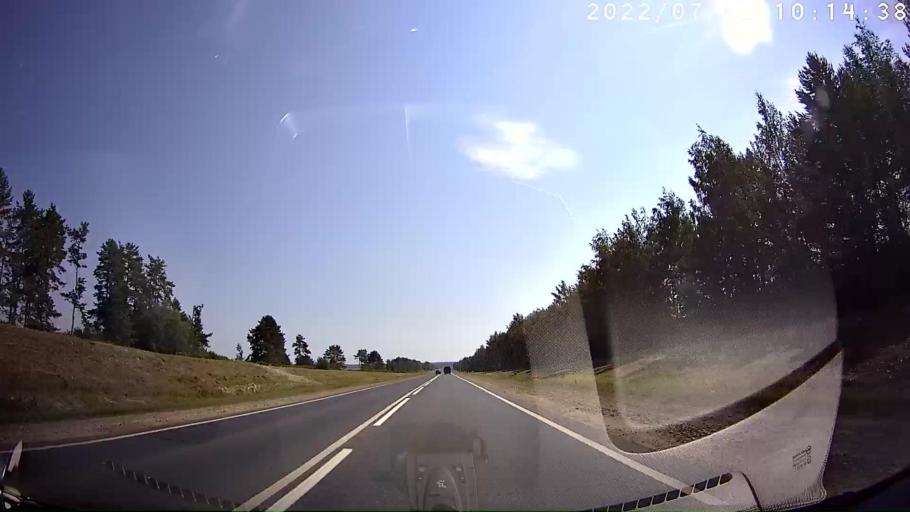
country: RU
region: Mariy-El
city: Sovetskiy
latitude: 56.7458
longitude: 48.2903
